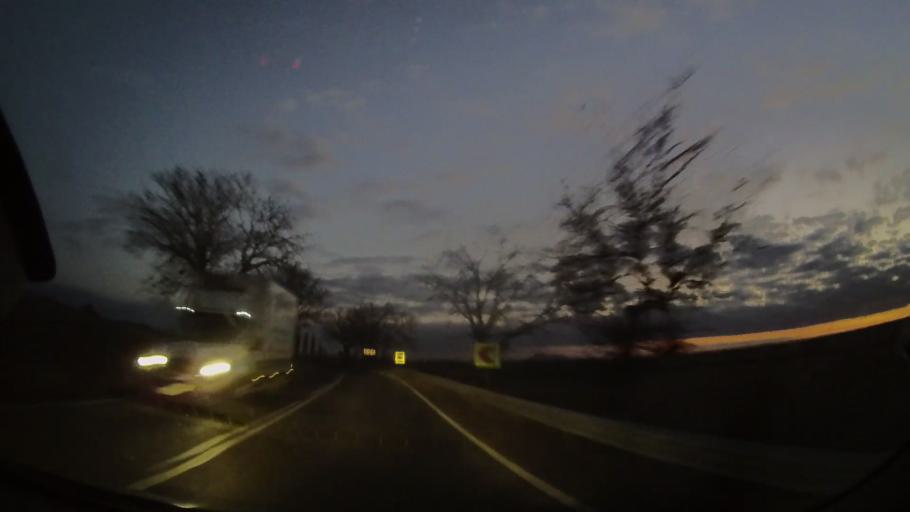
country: RO
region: Tulcea
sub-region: Comuna Frecatei
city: Cataloi
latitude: 45.0840
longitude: 28.7403
